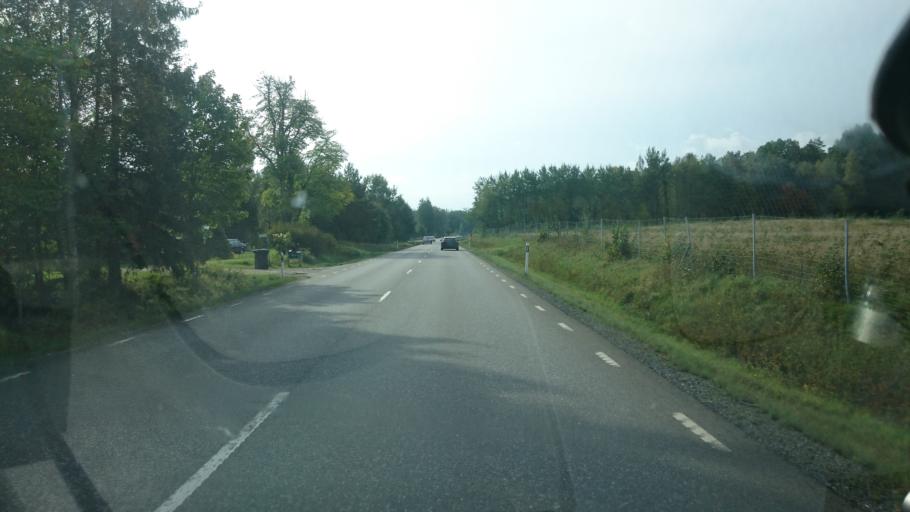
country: SE
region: Vaestra Goetaland
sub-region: Alingsas Kommun
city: Alingsas
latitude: 57.9919
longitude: 12.4415
